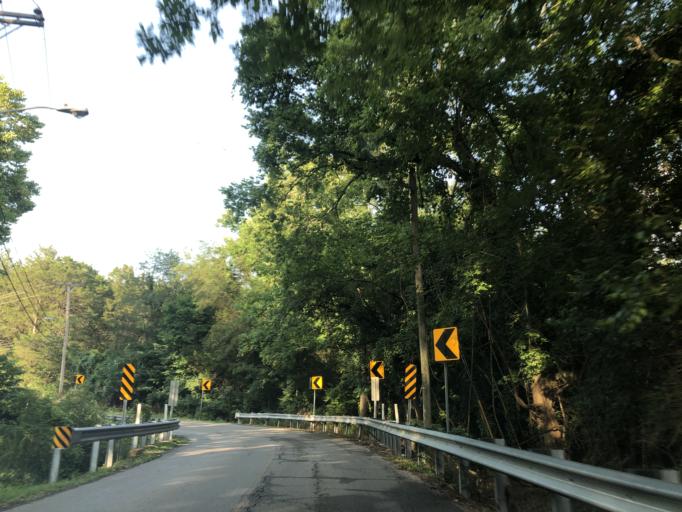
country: US
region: Tennessee
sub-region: Davidson County
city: Lakewood
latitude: 36.1457
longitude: -86.6539
